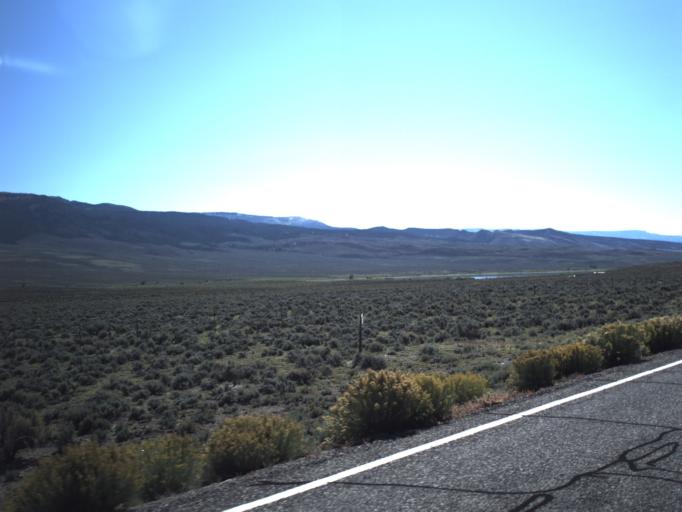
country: US
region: Utah
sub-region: Piute County
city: Junction
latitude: 38.2381
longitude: -111.9886
